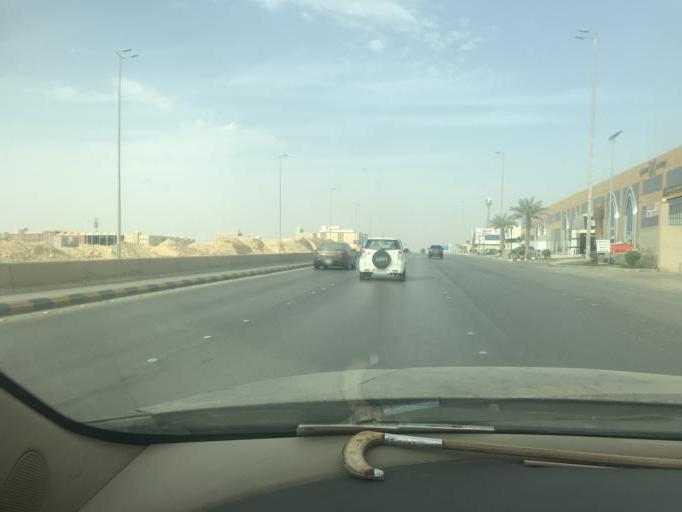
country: SA
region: Ar Riyad
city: Riyadh
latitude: 24.8155
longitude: 46.6824
